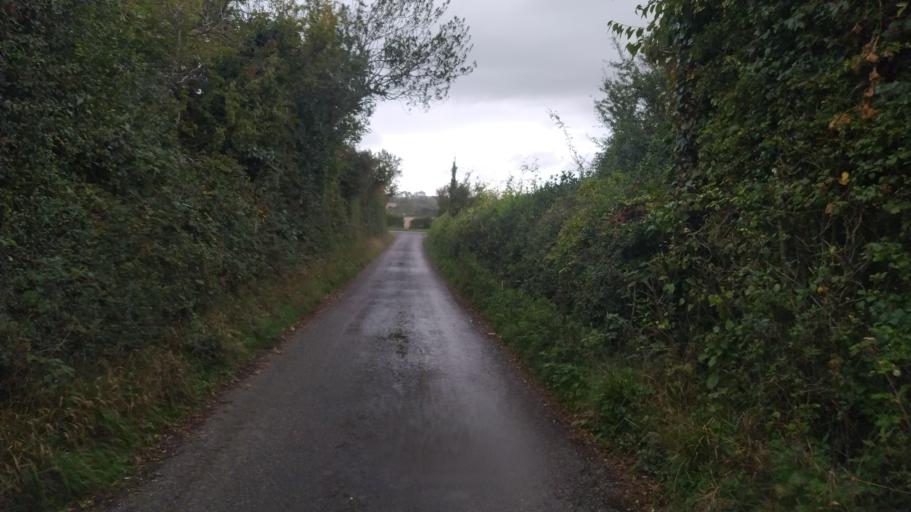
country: GB
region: England
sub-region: Dorset
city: Blandford Forum
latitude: 50.8159
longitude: -2.2016
